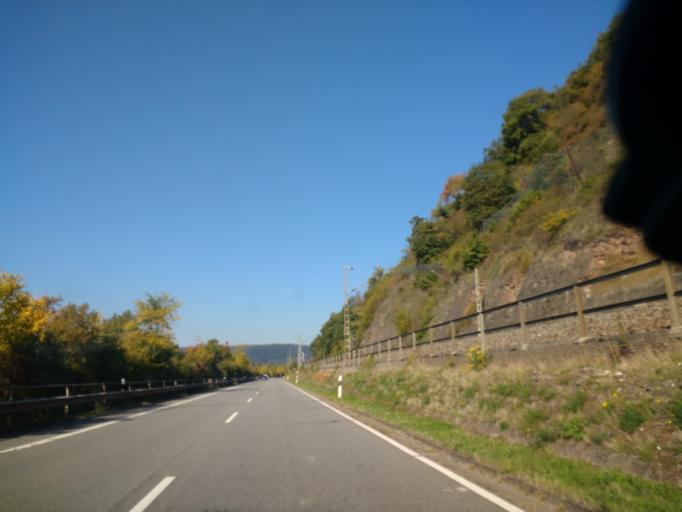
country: DE
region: Rheinland-Pfalz
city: Konz
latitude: 49.6857
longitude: 6.5669
